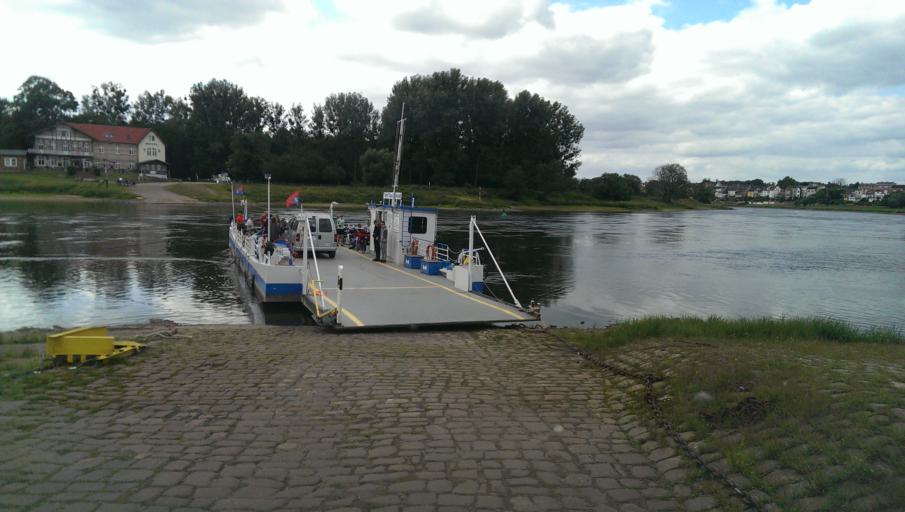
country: DE
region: Saxony-Anhalt
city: Coswig
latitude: 51.8769
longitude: 12.4538
